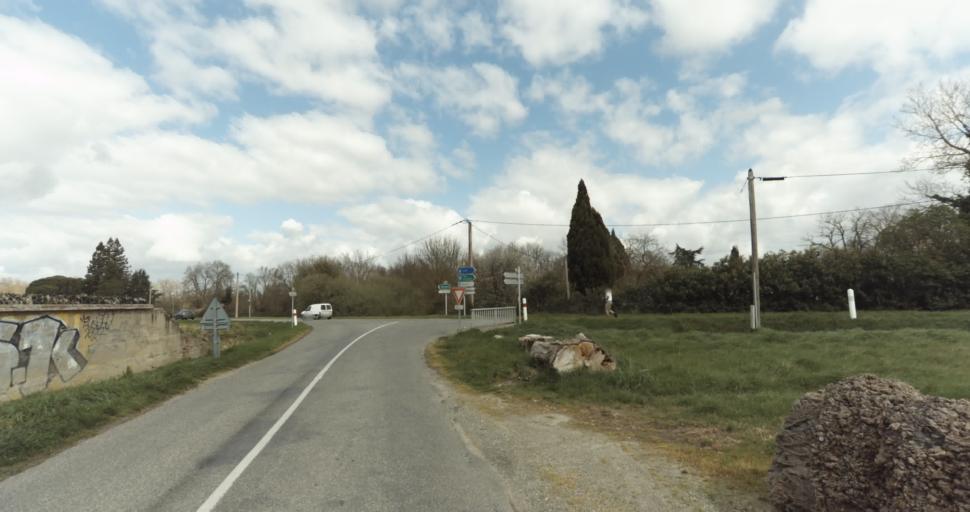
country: FR
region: Midi-Pyrenees
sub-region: Departement de la Haute-Garonne
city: Auterive
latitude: 43.3374
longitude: 1.4799
